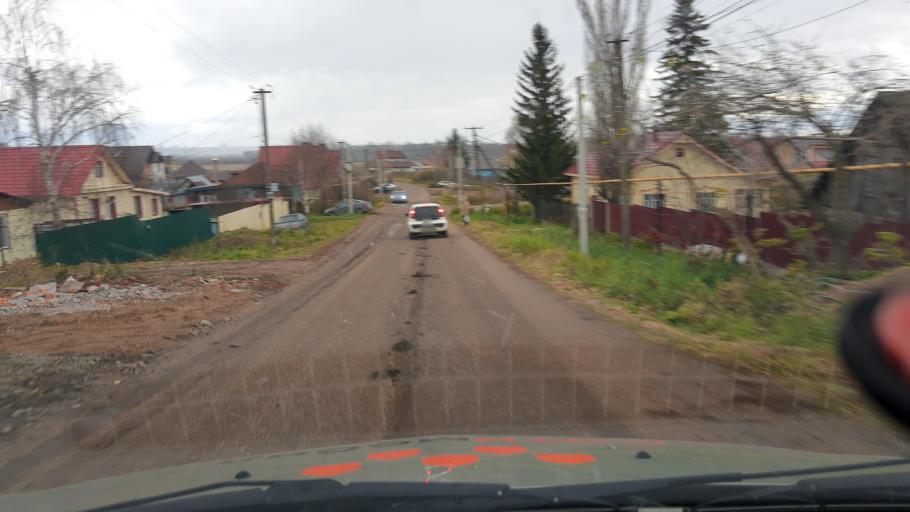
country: RU
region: Bashkortostan
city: Mikhaylovka
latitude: 54.8240
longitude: 55.9076
